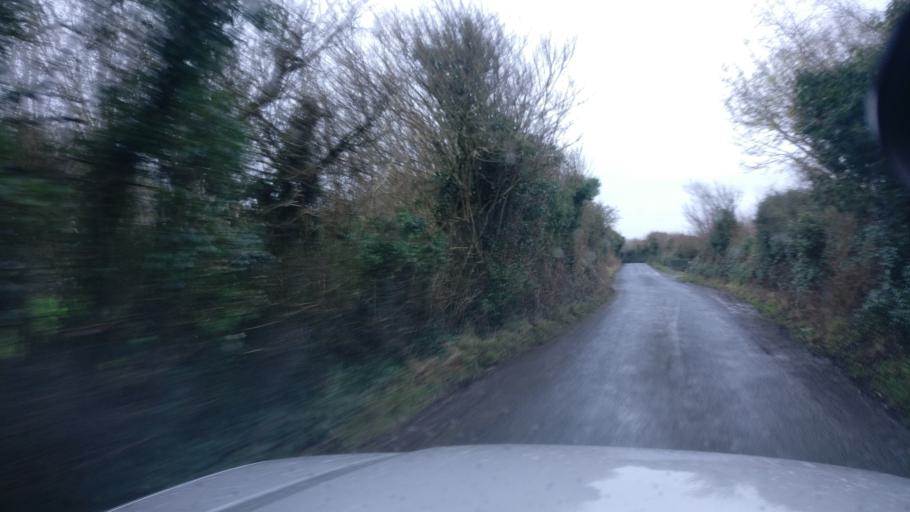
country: IE
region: Connaught
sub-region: County Galway
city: Loughrea
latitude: 53.2103
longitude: -8.6667
